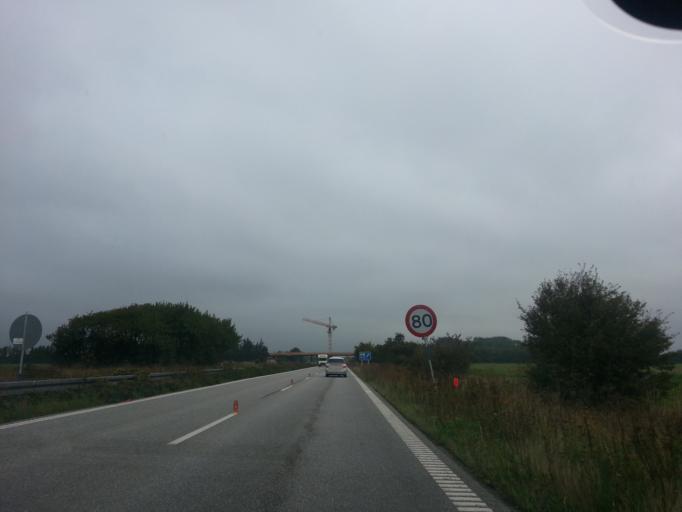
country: DK
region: Zealand
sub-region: Lolland Kommune
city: Holeby
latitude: 54.7131
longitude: 11.4262
